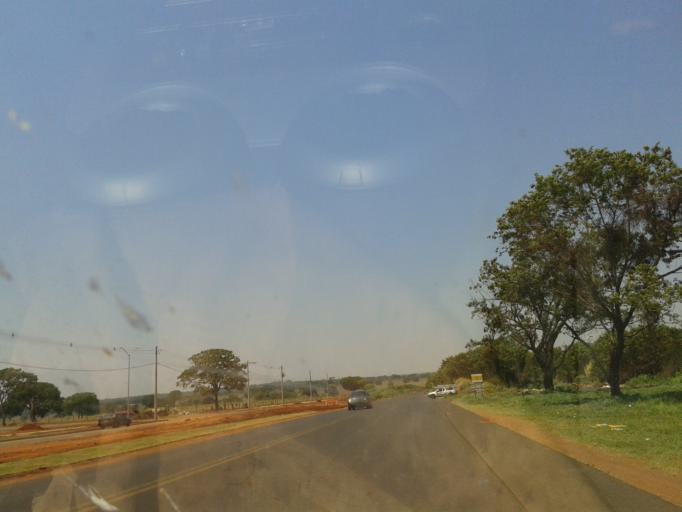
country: BR
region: Minas Gerais
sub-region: Uberlandia
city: Uberlandia
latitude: -18.9602
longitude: -48.3068
